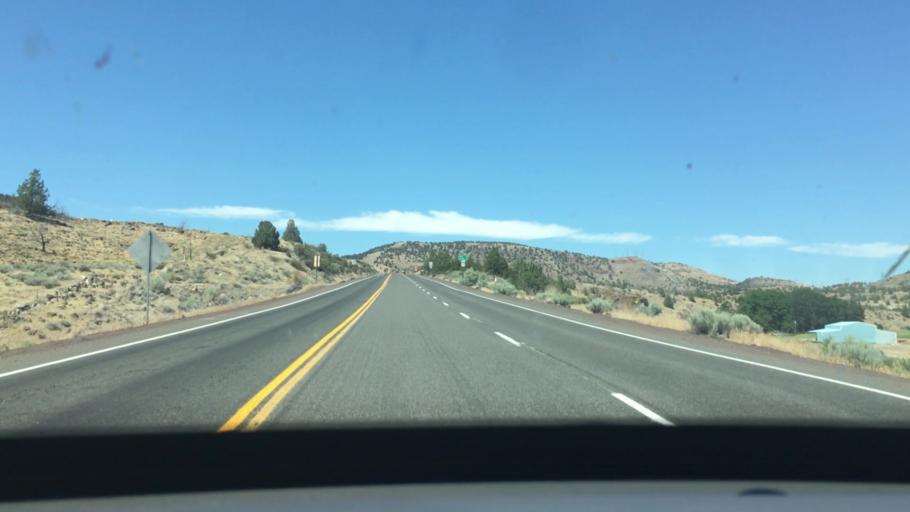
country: US
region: Oregon
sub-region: Jefferson County
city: Madras
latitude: 44.8171
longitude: -120.9312
